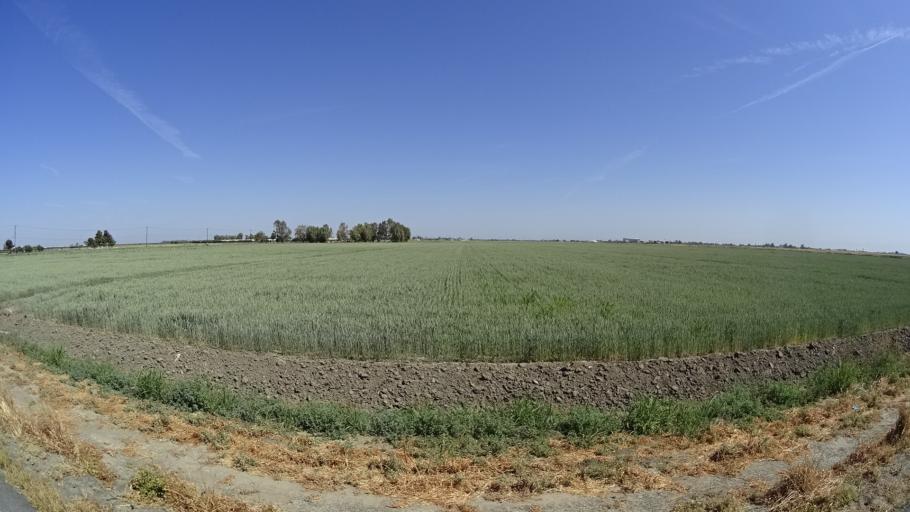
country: US
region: California
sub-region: Kings County
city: Stratford
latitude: 36.2113
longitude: -119.7780
